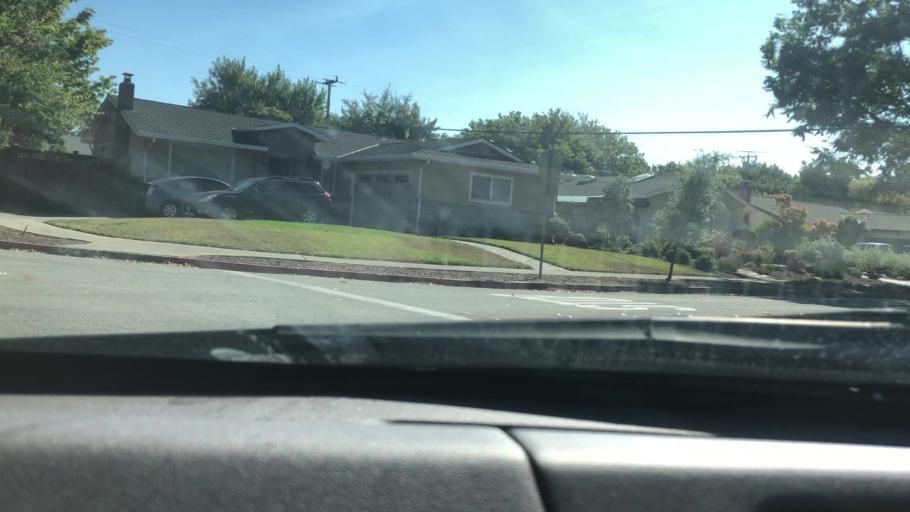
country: US
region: California
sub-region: Santa Clara County
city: Campbell
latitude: 37.3007
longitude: -121.9914
